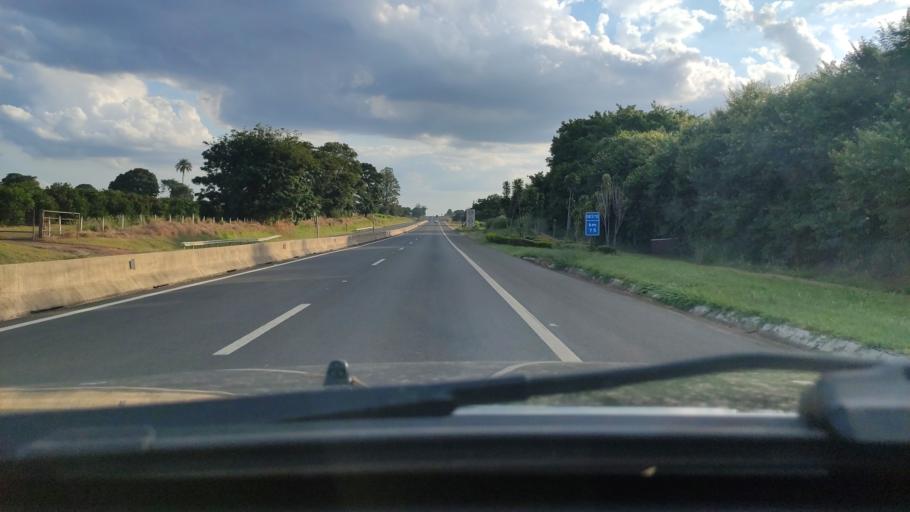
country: BR
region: Sao Paulo
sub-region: Artur Nogueira
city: Artur Nogueira
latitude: -22.4601
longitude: -47.0995
